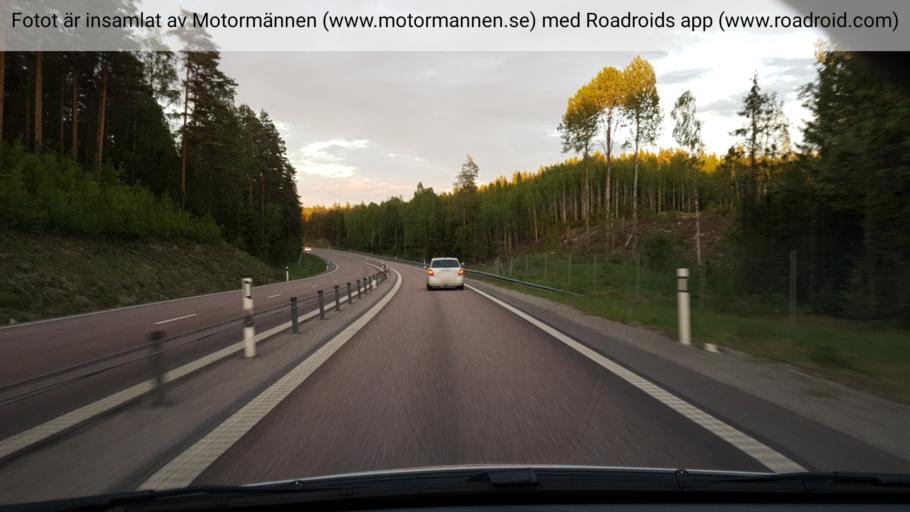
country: SE
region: Vaestmanland
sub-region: Fagersta Kommun
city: Fagersta
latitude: 59.9421
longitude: 15.8695
